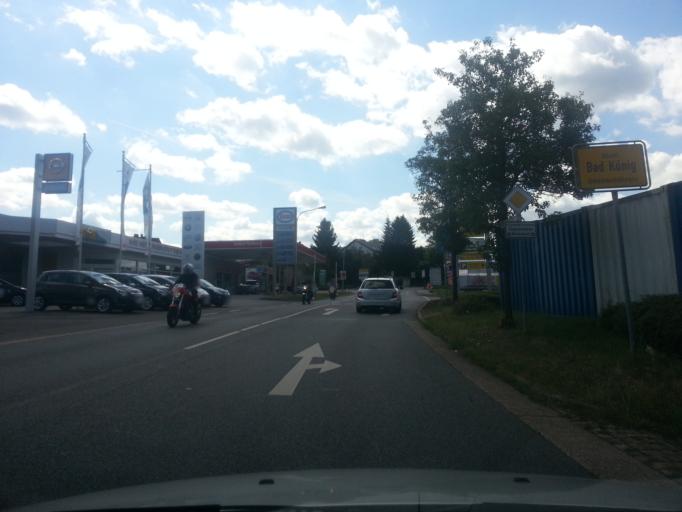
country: DE
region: Hesse
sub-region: Regierungsbezirk Darmstadt
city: Bad Konig
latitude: 49.7480
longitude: 9.0028
